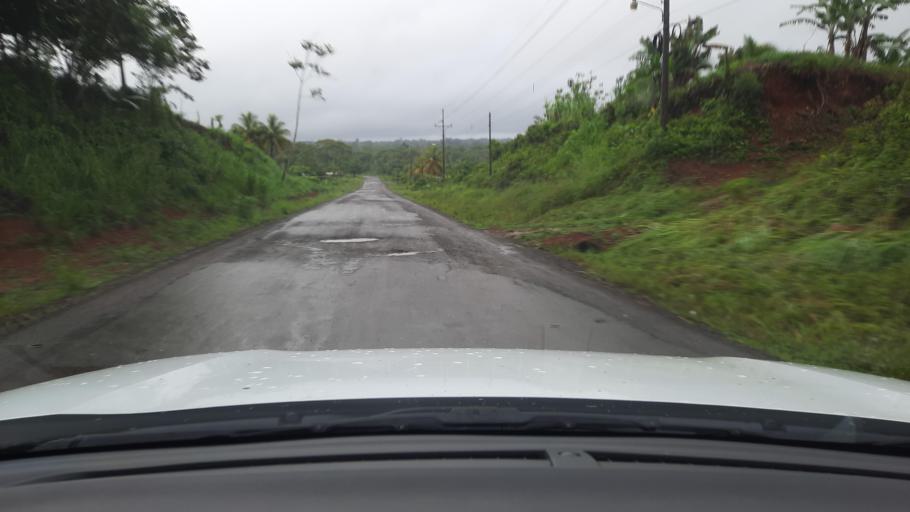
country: NI
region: Rivas
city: Cardenas
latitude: 11.0262
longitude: -85.3625
